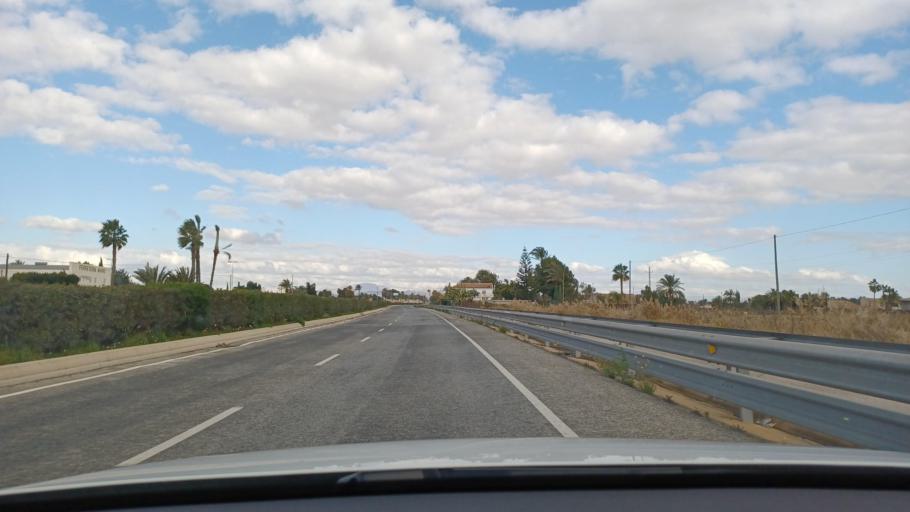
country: ES
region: Valencia
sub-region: Provincia de Alicante
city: Elche
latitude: 38.1897
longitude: -0.7010
